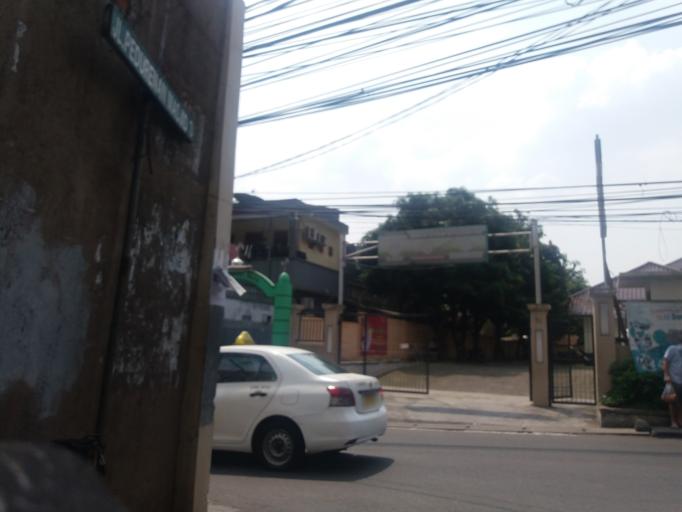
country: ID
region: Jakarta Raya
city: Jakarta
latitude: -6.2214
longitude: 106.8257
